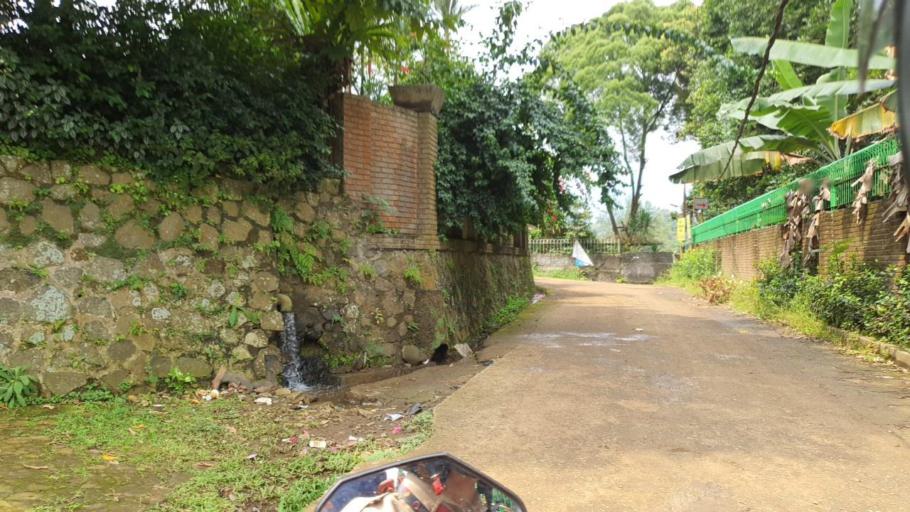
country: ID
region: West Java
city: Caringin
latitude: -6.6550
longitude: 106.8843
